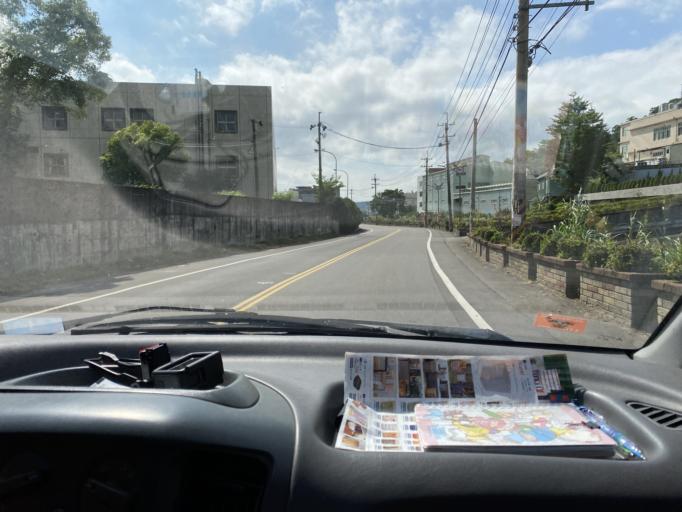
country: TW
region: Taiwan
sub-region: Hsinchu
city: Zhubei
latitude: 24.7369
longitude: 121.1258
